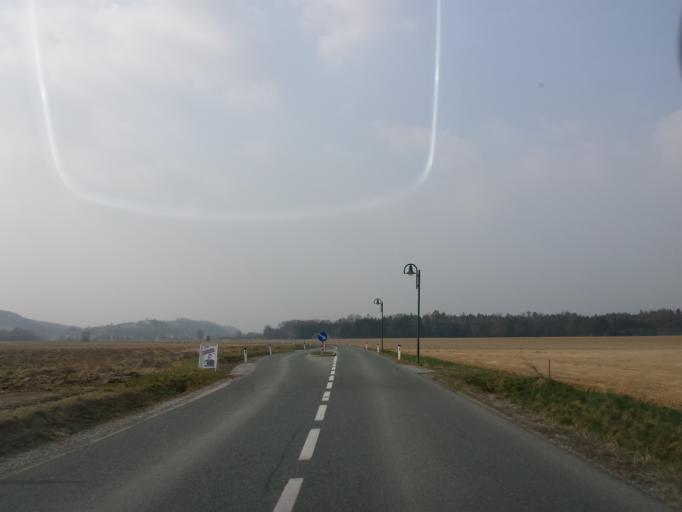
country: AT
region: Burgenland
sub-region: Politischer Bezirk Jennersdorf
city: Konigsdorf
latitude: 47.0003
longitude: 16.1356
